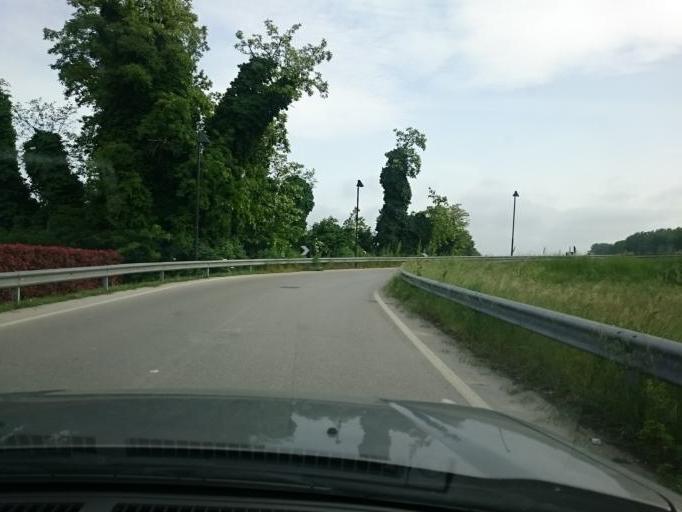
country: IT
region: Veneto
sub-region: Provincia di Venezia
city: Mestre
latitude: 45.4338
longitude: 12.2030
